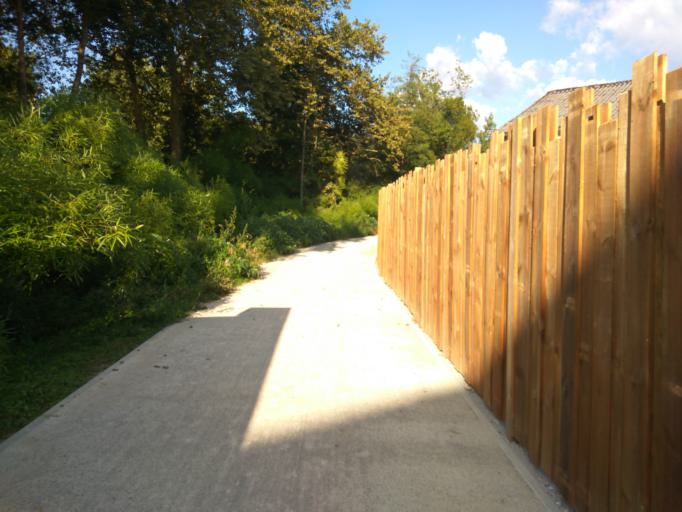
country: FR
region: Aquitaine
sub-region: Departement des Pyrenees-Atlantiques
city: Jurancon
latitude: 43.2922
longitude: -0.3773
